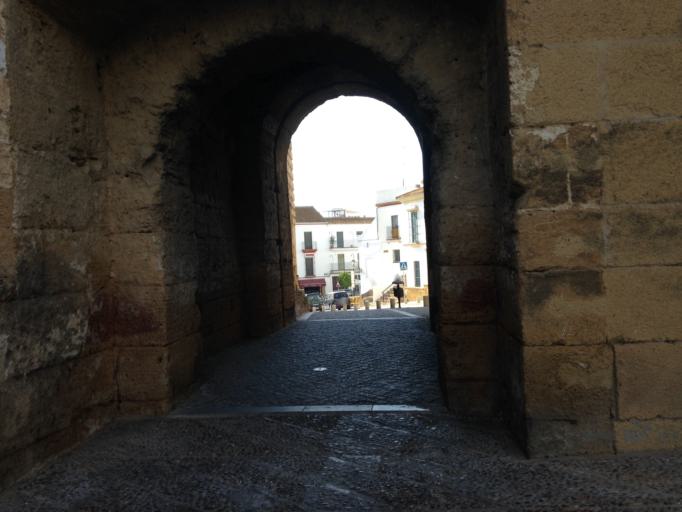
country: ES
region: Andalusia
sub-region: Provincia de Sevilla
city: Carmona
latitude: 37.4714
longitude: -5.6409
